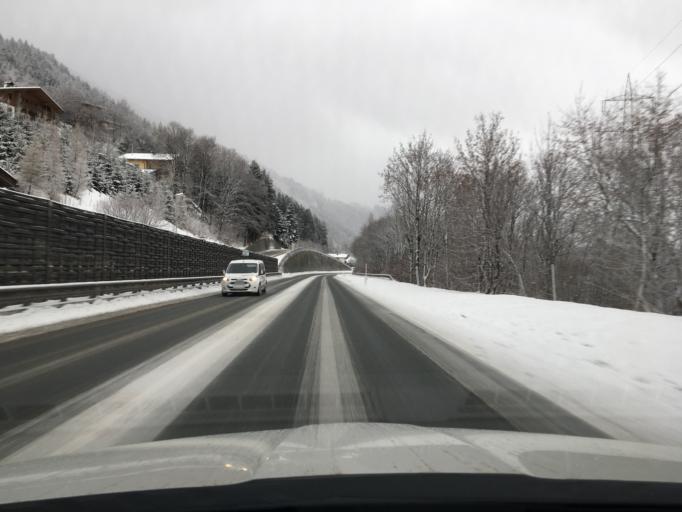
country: AT
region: Tyrol
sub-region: Politischer Bezirk Schwaz
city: Rohrberg
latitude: 47.2472
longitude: 11.9013
